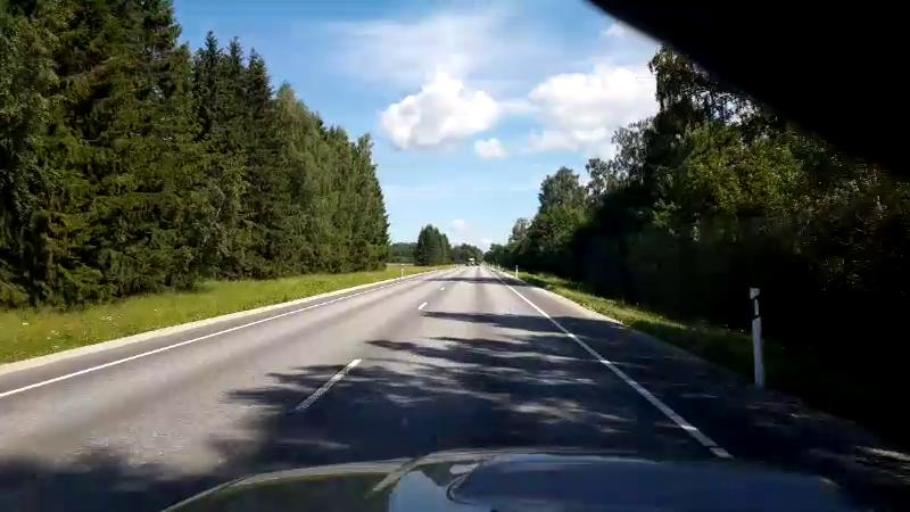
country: EE
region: Jaervamaa
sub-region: Paide linn
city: Paide
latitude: 58.9786
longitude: 25.6669
